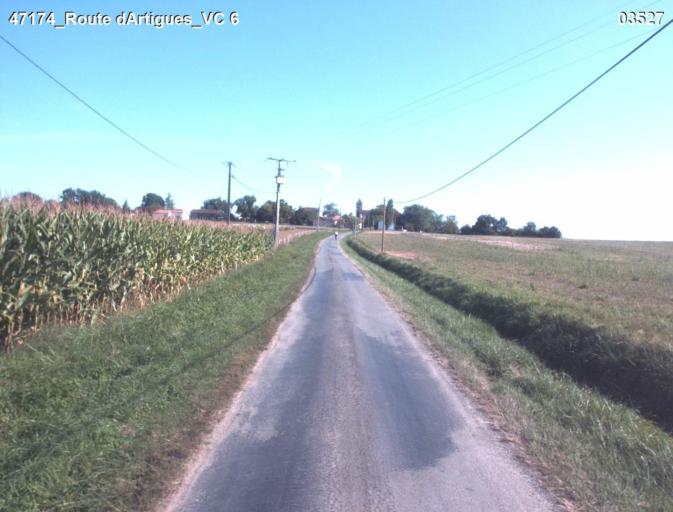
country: FR
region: Aquitaine
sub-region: Departement du Lot-et-Garonne
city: Mezin
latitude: 44.0378
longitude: 0.3374
